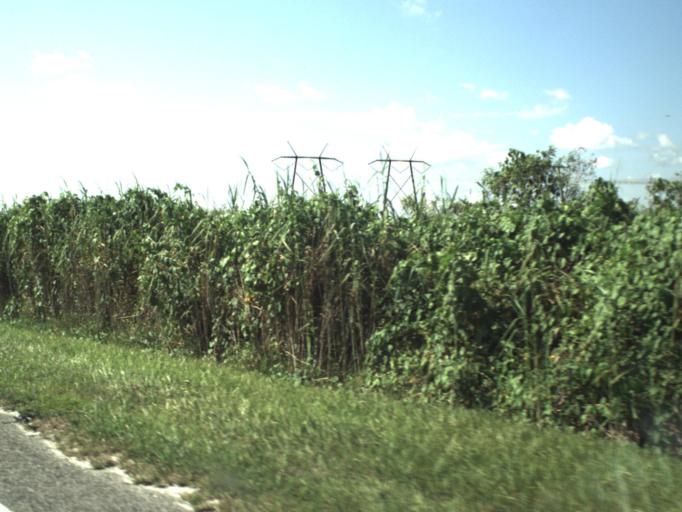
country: US
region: Florida
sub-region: Broward County
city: Weston
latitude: 26.2843
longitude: -80.4990
